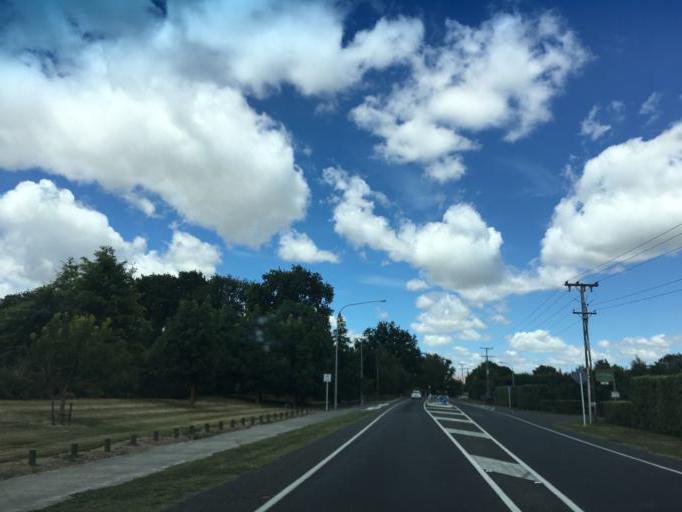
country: NZ
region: Hawke's Bay
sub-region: Hastings District
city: Hastings
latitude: -39.6534
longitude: 176.8752
